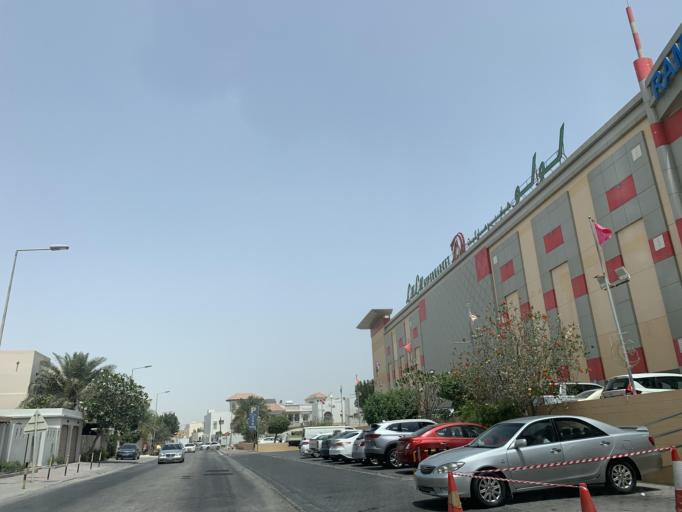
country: BH
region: Northern
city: Madinat `Isa
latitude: 26.1625
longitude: 50.5225
